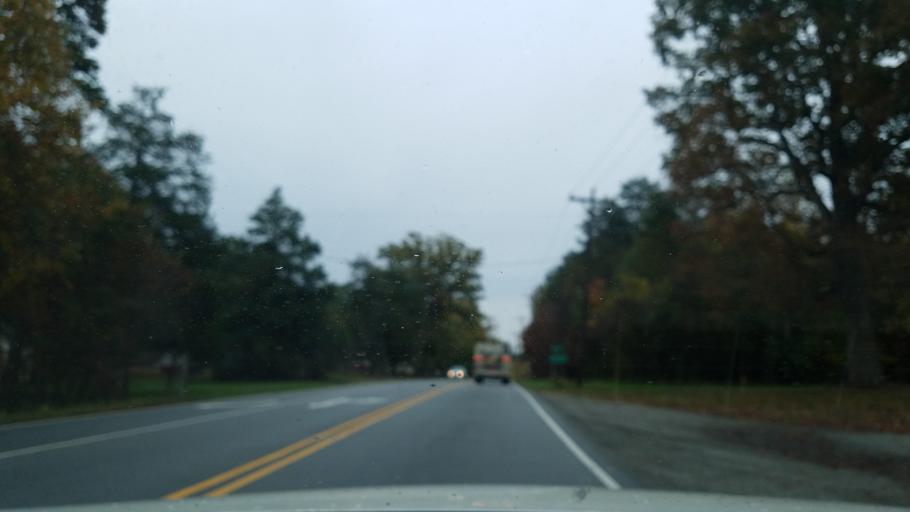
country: US
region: North Carolina
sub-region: Guilford County
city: Pleasant Garden
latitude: 35.9922
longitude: -79.7930
